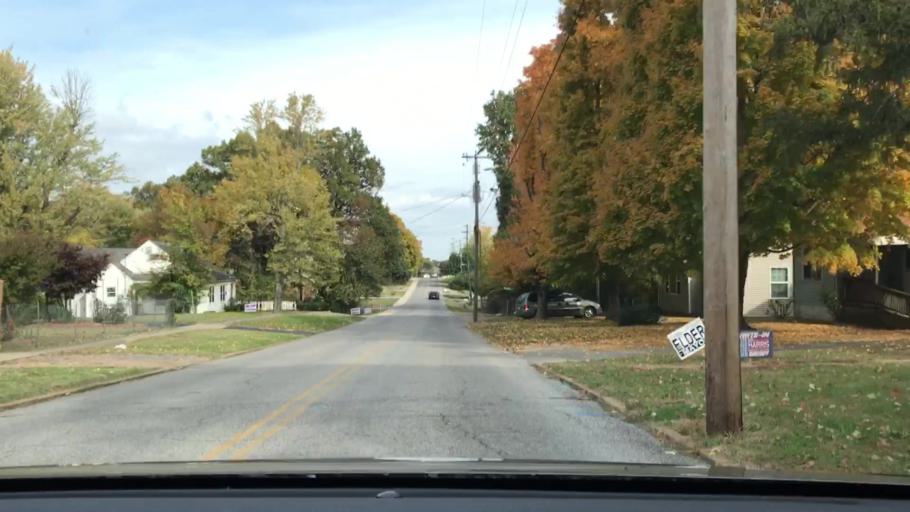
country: US
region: Kentucky
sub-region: Graves County
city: Mayfield
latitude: 36.7441
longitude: -88.6495
